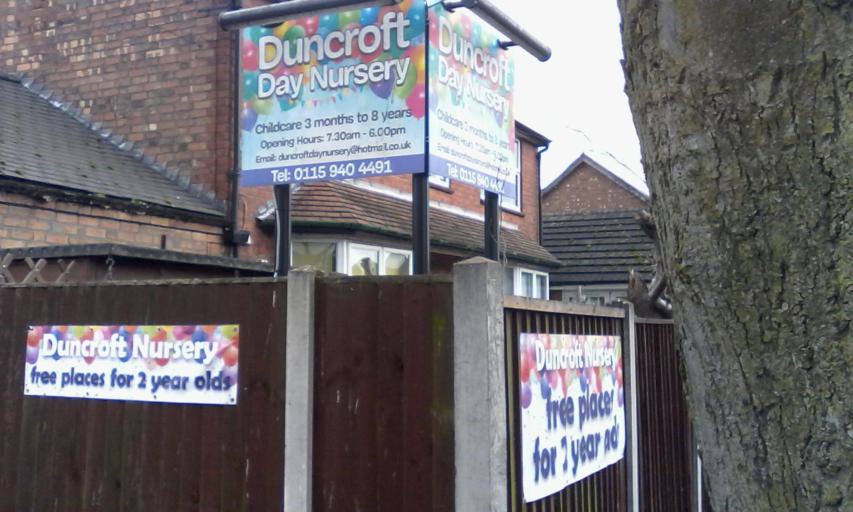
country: GB
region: England
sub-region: Nottinghamshire
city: Burton Joyce
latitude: 52.9733
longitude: -1.0810
